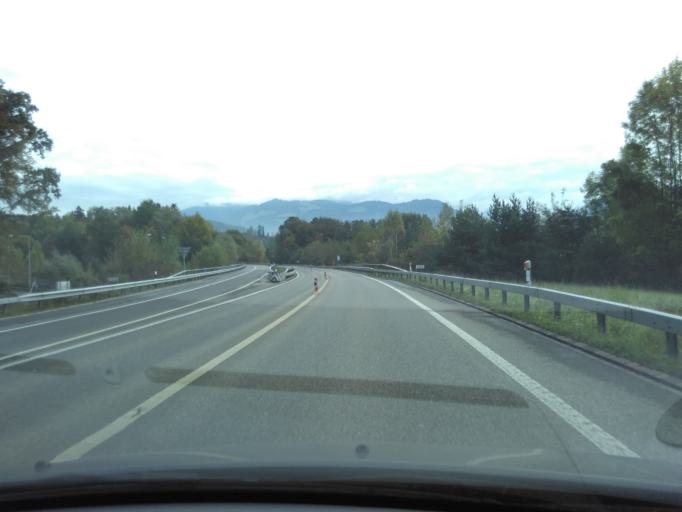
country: CH
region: Zurich
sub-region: Bezirk Hinwil
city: Rueti / Dorfzentrum, Suedl. Teil
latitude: 47.2314
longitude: 8.8658
